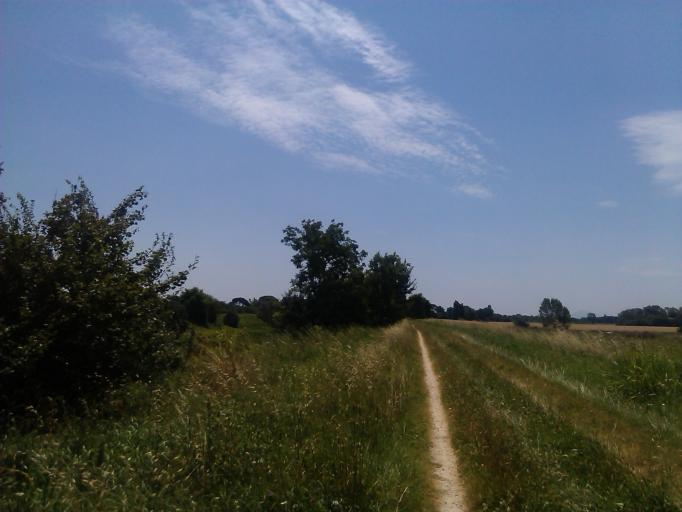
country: IT
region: Tuscany
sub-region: Province of Arezzo
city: Cesa
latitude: 43.3263
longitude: 11.8328
